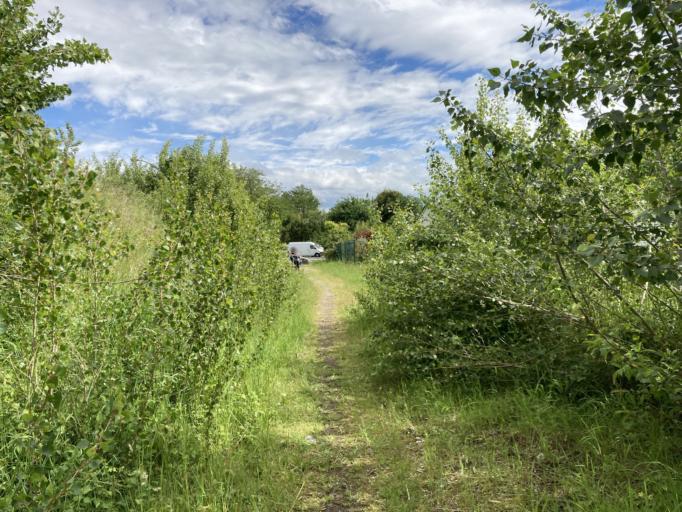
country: FR
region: Aquitaine
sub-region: Departement des Pyrenees-Atlantiques
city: Billere
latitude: 43.2989
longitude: -0.4108
